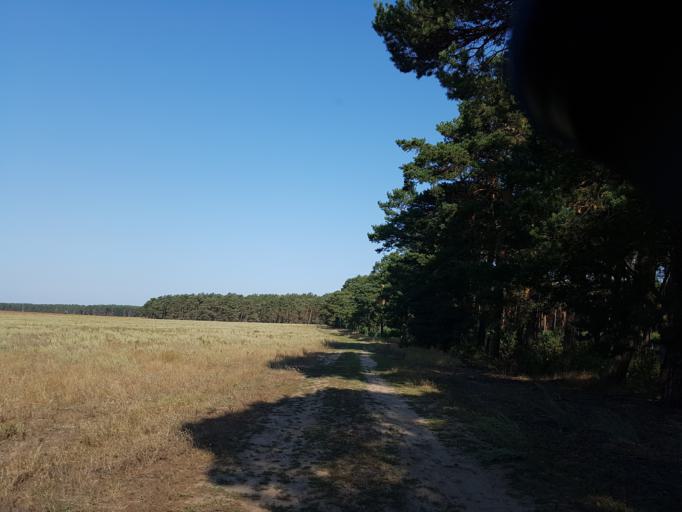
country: DE
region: Brandenburg
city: Wollin
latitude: 52.2491
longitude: 12.5090
